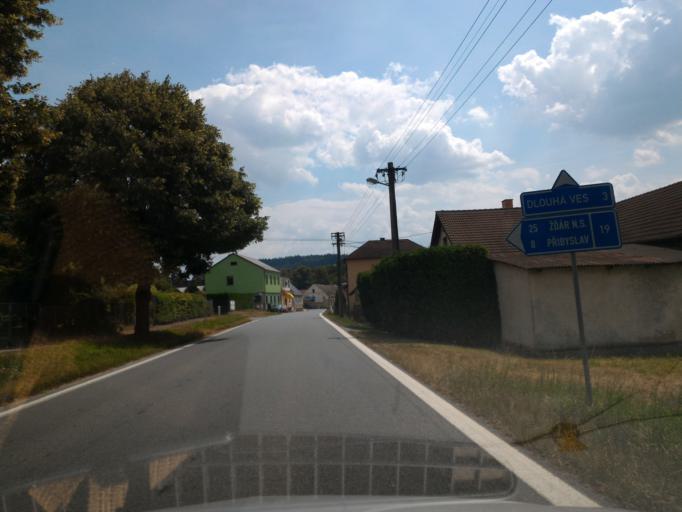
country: CZ
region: Vysocina
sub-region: Okres Havlickuv Brod
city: Havlickuv Brod
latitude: 49.6065
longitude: 15.6472
